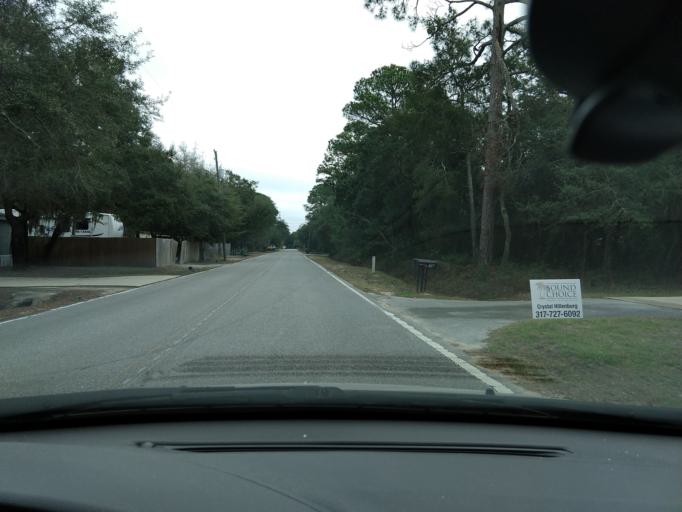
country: US
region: Florida
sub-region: Walton County
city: Miramar Beach
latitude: 30.4051
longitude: -86.3071
